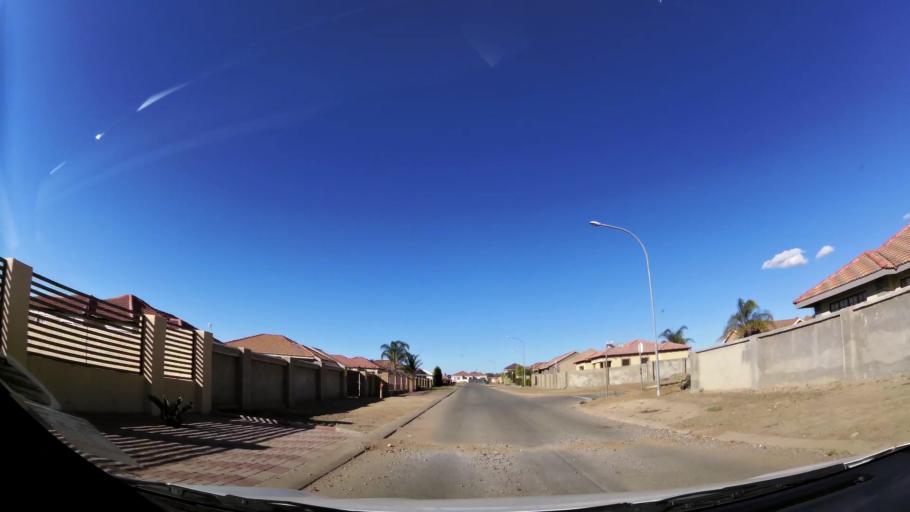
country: ZA
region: Limpopo
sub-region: Capricorn District Municipality
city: Polokwane
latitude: -23.9044
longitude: 29.5076
